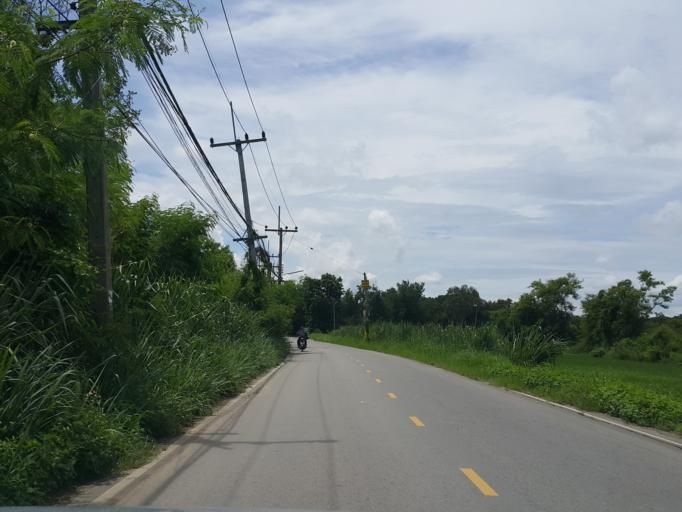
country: TH
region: Chiang Mai
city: San Kamphaeng
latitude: 18.7592
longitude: 99.0995
